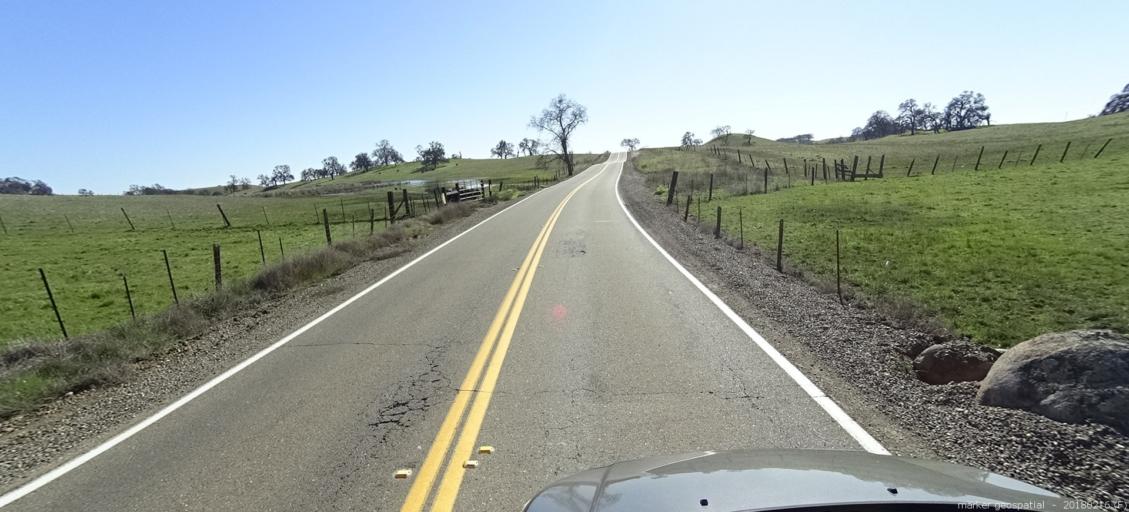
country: US
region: California
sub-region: Sacramento County
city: Rancho Murieta
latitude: 38.5911
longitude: -121.1295
